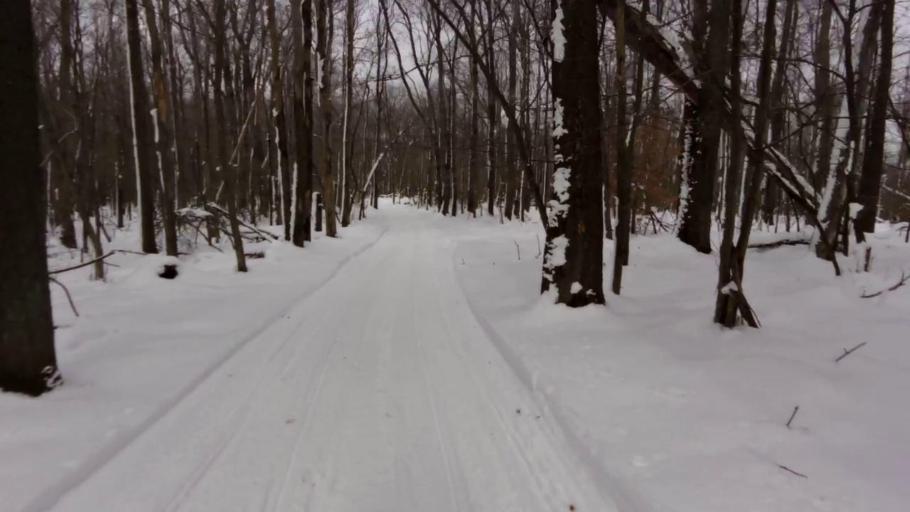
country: US
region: Pennsylvania
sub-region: McKean County
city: Bradford
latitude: 42.0273
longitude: -78.7408
